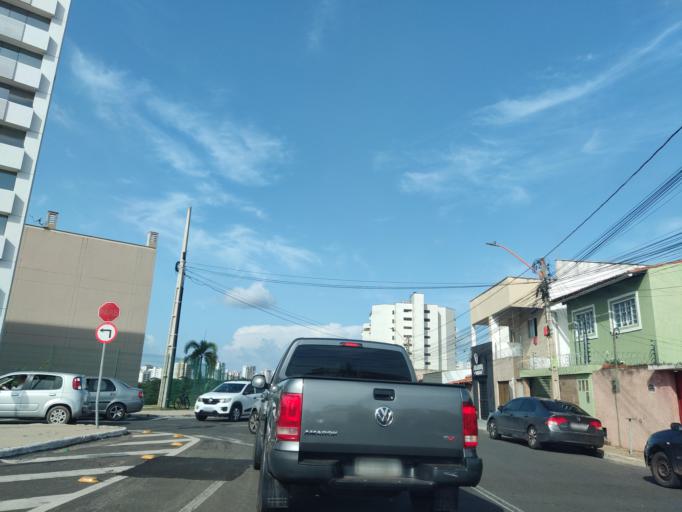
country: BR
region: Piaui
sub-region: Teresina
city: Teresina
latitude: -5.0790
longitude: -42.8021
